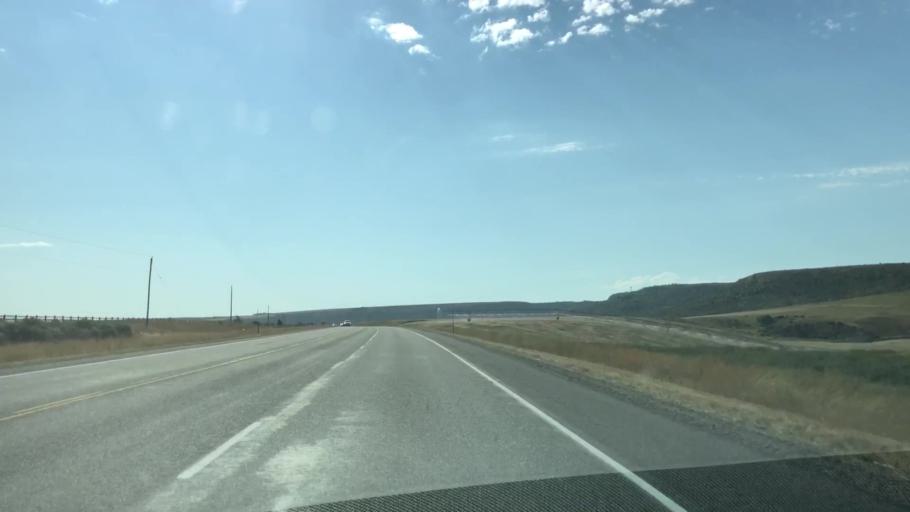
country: US
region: Idaho
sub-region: Madison County
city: Rexburg
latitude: 43.5931
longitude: -111.6403
